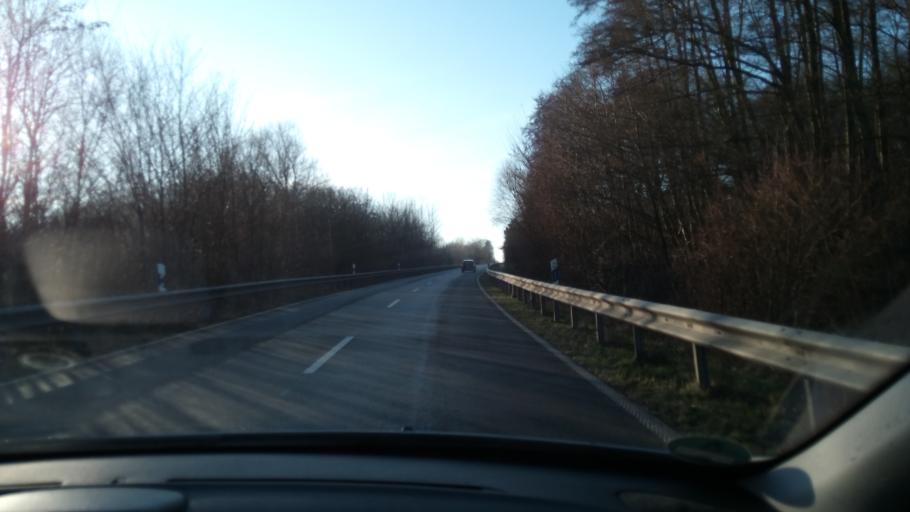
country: DE
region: Schleswig-Holstein
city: Dalldorf
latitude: 53.4289
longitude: 10.5992
